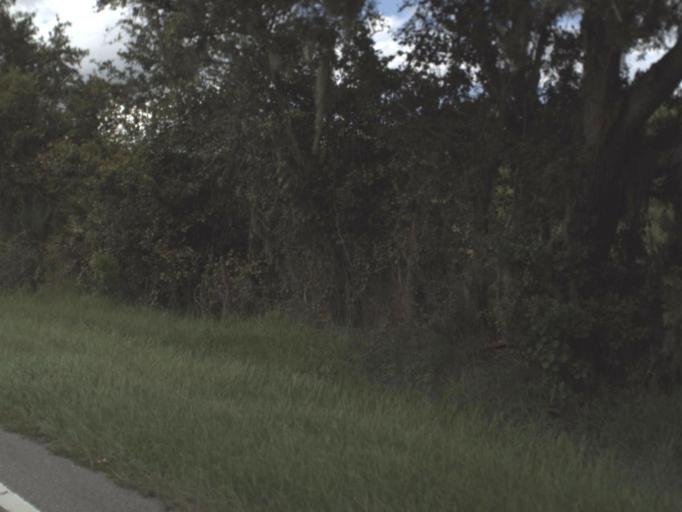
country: US
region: Florida
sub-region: Hillsborough County
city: Balm
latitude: 27.6156
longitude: -82.0899
